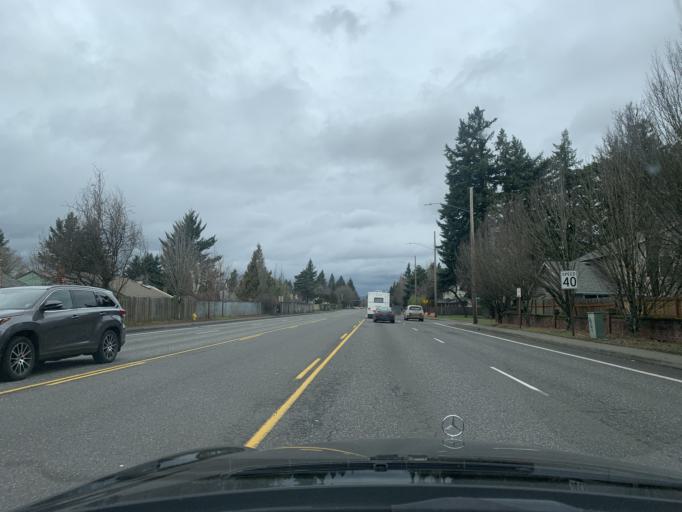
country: US
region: Oregon
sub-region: Multnomah County
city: Troutdale
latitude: 45.5229
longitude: -122.3984
